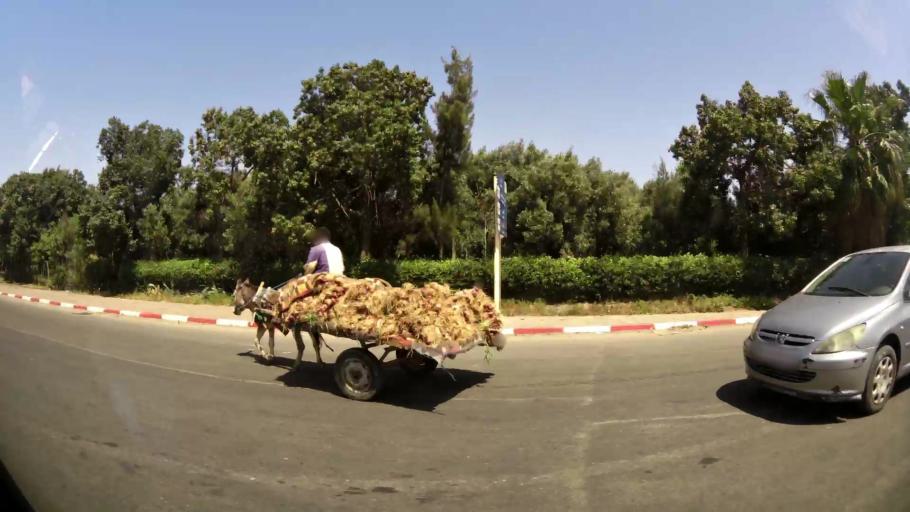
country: MA
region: Souss-Massa-Draa
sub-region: Inezgane-Ait Mellou
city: Inezgane
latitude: 30.3522
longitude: -9.5057
